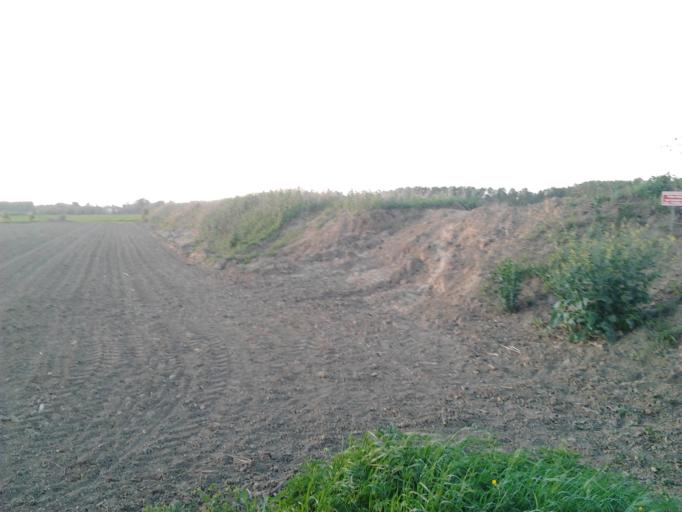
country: FR
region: Midi-Pyrenees
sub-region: Departement de la Haute-Garonne
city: Ondes
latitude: 43.7662
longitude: 1.3152
